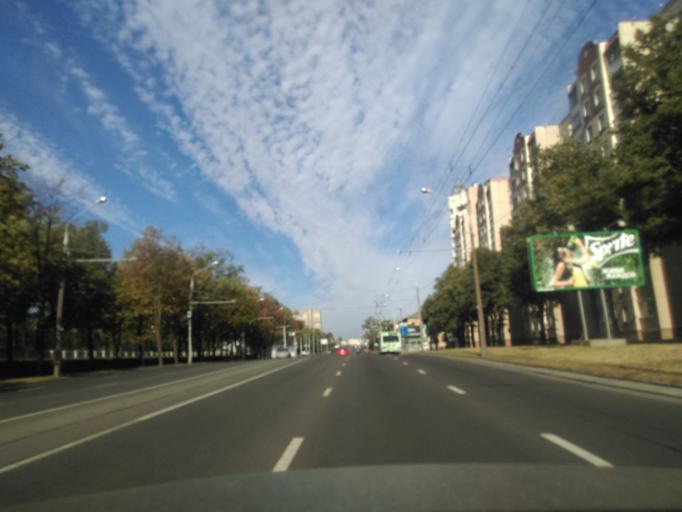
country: BY
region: Minsk
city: Minsk
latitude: 53.8826
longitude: 27.5955
